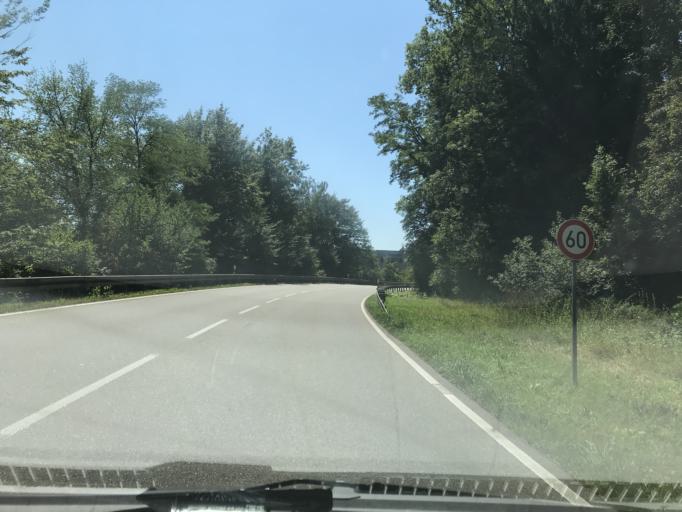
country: DE
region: Baden-Wuerttemberg
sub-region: Freiburg Region
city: Schworstadt
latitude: 47.5876
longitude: 7.9101
